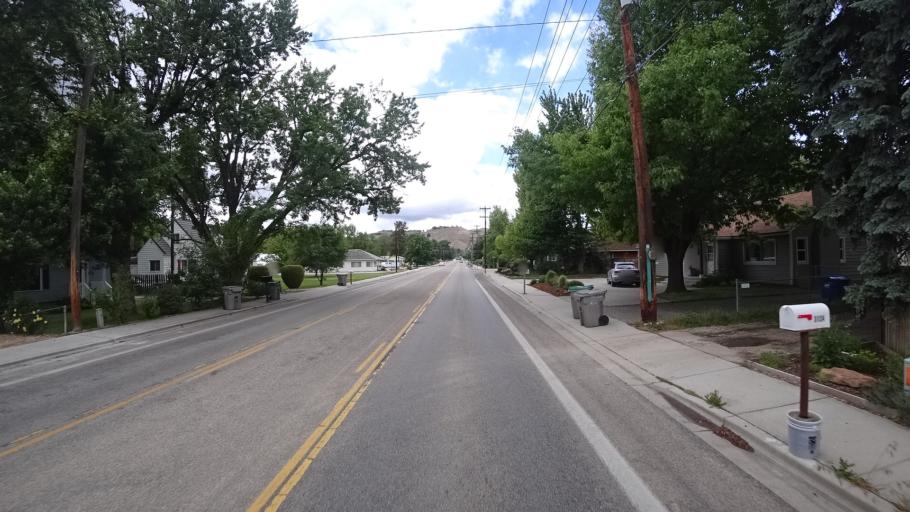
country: US
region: Idaho
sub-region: Ada County
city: Garden City
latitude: 43.6489
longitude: -116.2334
